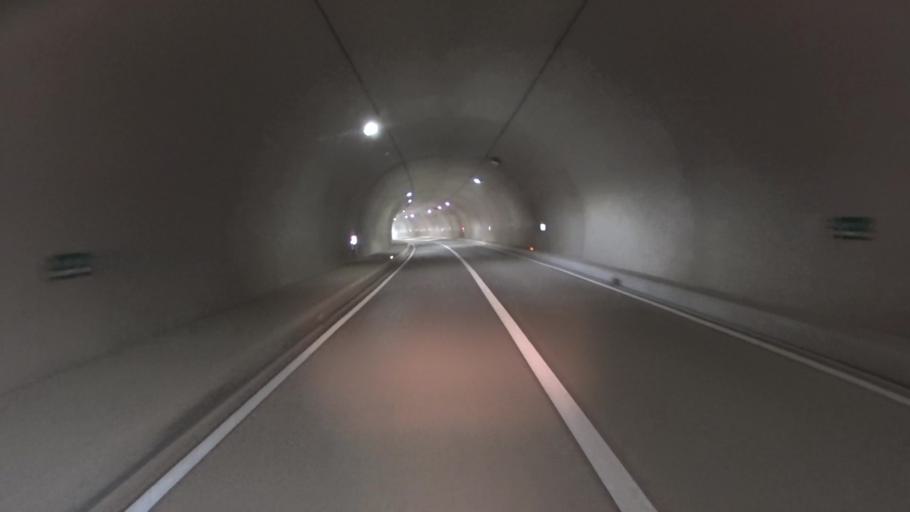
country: JP
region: Kyoto
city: Miyazu
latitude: 35.7400
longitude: 135.2551
